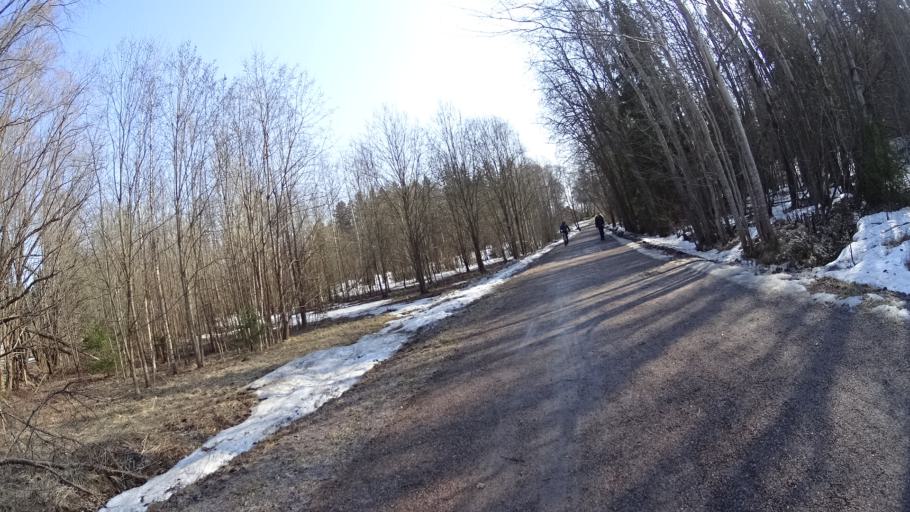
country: FI
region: Uusimaa
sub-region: Helsinki
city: Espoo
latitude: 60.2102
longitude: 24.6455
